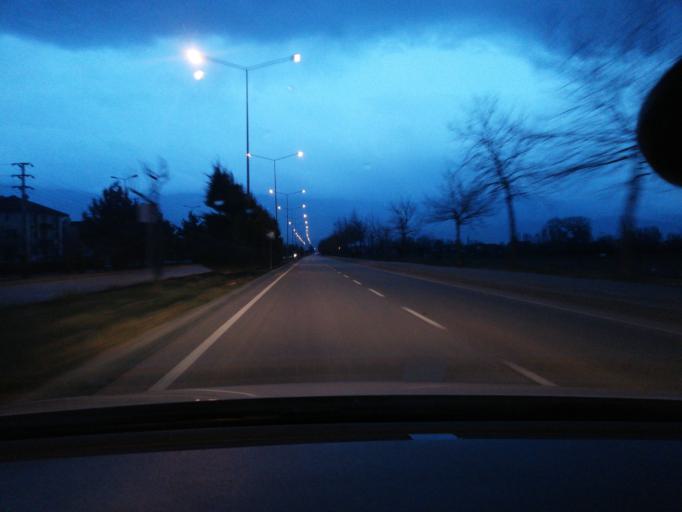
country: TR
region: Bolu
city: Bolu
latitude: 40.7193
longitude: 31.6138
